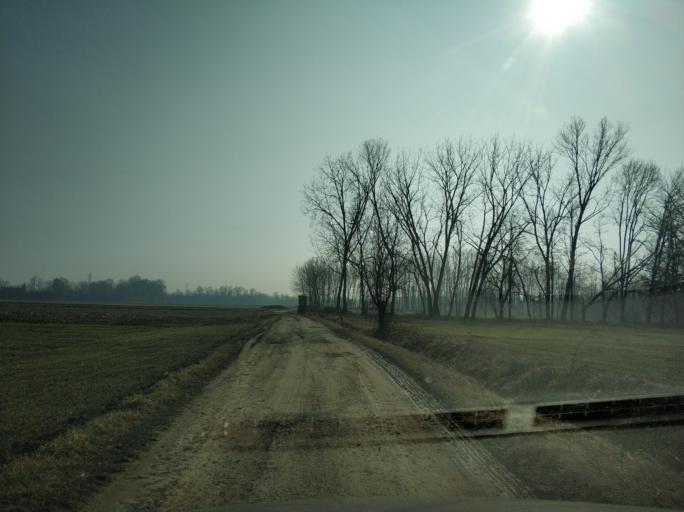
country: IT
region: Piedmont
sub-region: Provincia di Torino
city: Rivarossa
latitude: 45.2511
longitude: 7.7304
